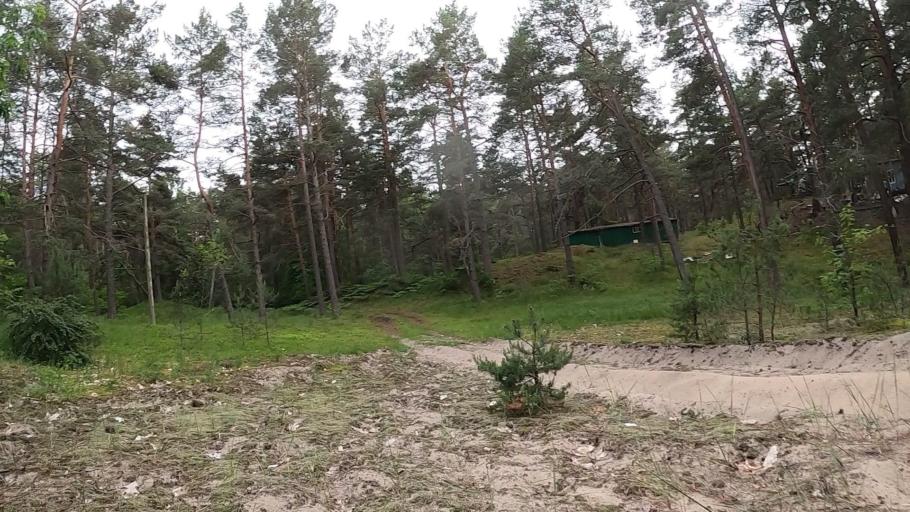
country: LV
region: Riga
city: Jaunciems
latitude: 57.0872
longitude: 24.1624
